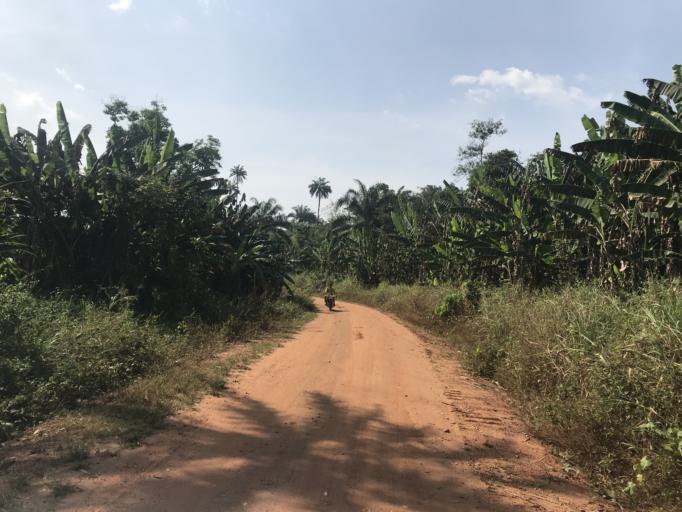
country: NG
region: Osun
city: Ilesa
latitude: 7.6309
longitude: 4.6856
